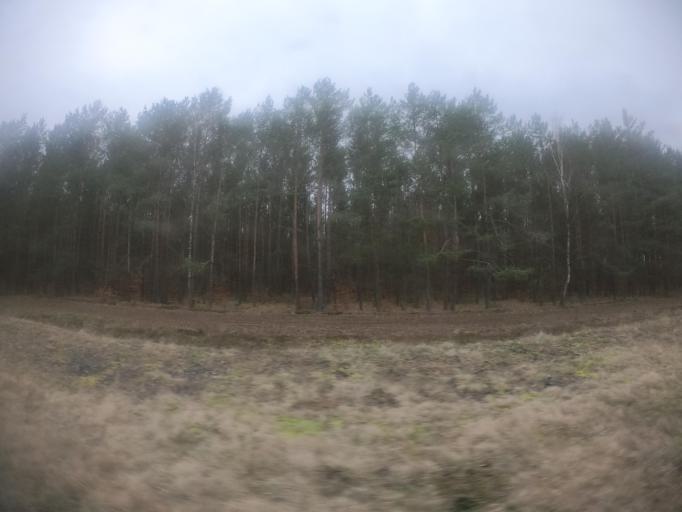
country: PL
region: West Pomeranian Voivodeship
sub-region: Powiat szczecinecki
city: Bialy Bor
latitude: 53.8044
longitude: 16.8654
